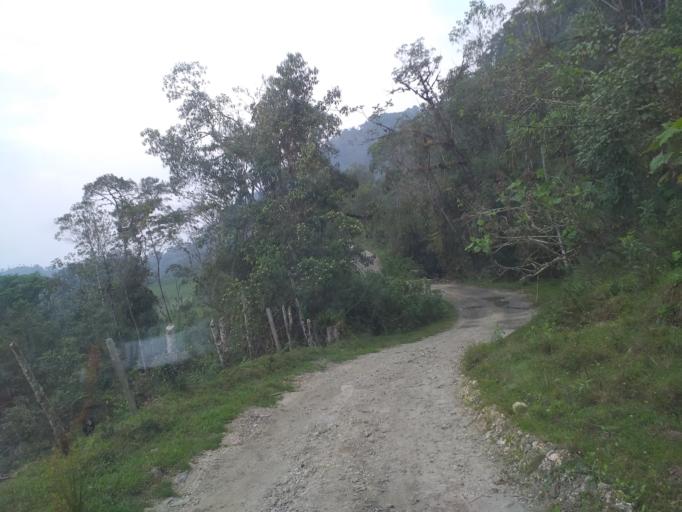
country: CO
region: Boyaca
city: Aquitania
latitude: 5.3221
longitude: -72.9398
